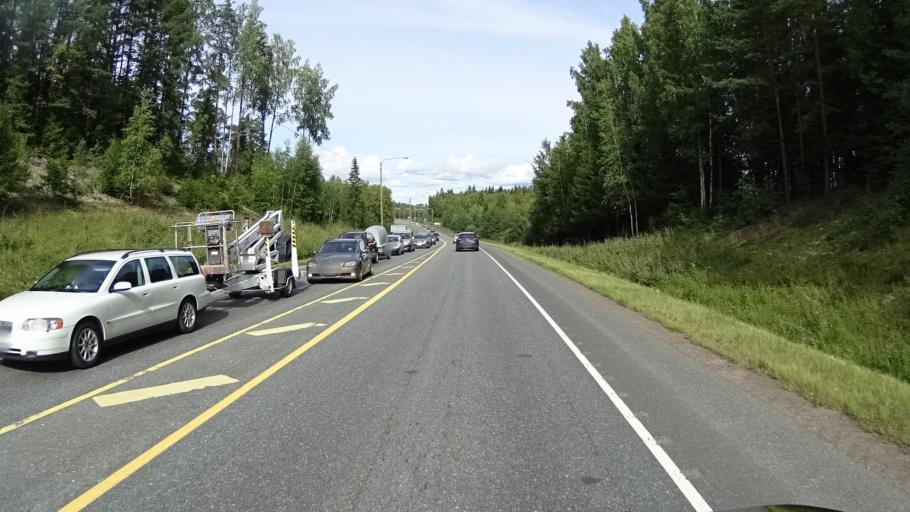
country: FI
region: Pirkanmaa
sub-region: Tampere
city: Haemeenkyroe
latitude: 61.6778
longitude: 23.1612
